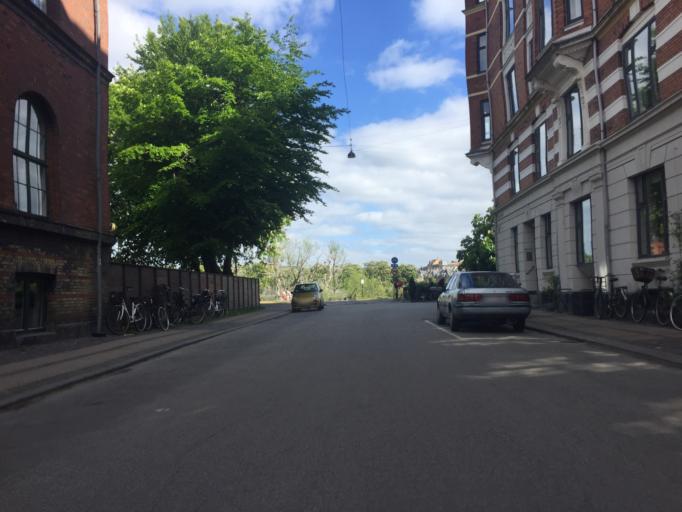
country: DK
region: Capital Region
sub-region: Kobenhavn
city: Copenhagen
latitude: 55.6949
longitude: 12.5723
